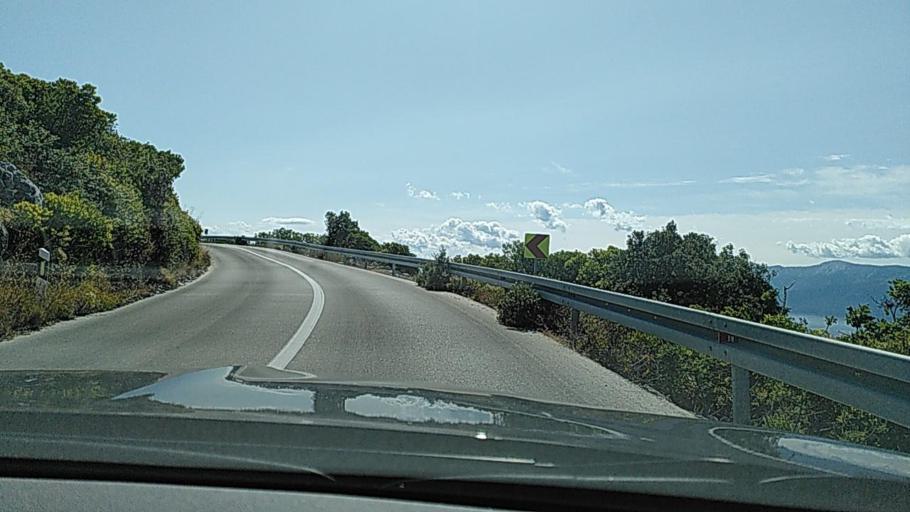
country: HR
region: Dubrovacko-Neretvanska
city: Orebic
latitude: 43.1225
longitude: 17.1108
